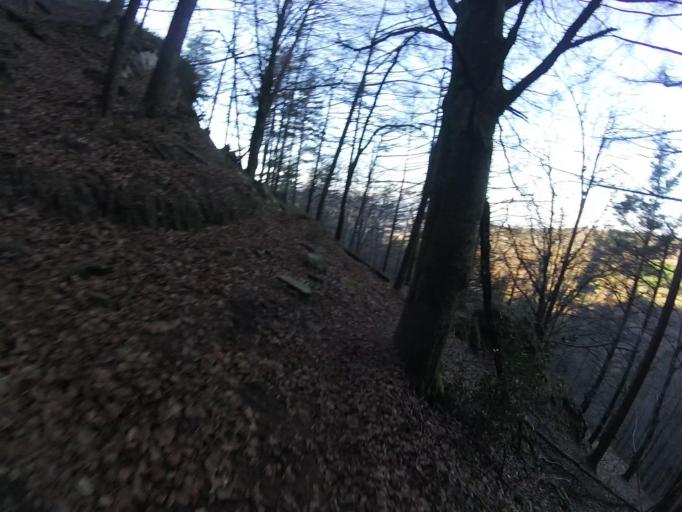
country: ES
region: Basque Country
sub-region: Provincia de Guipuzcoa
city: Irun
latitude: 43.2898
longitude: -1.7901
